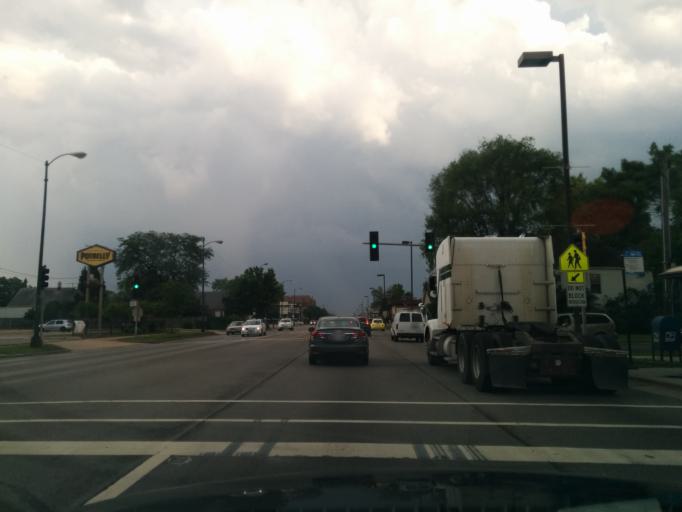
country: US
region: Illinois
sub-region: Cook County
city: Summit
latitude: 41.7886
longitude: -87.8015
